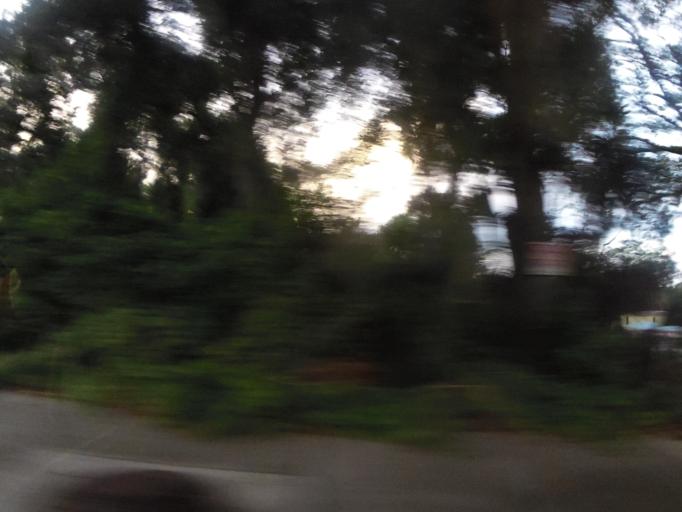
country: US
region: Florida
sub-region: Duval County
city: Jacksonville
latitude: 30.3669
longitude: -81.5605
